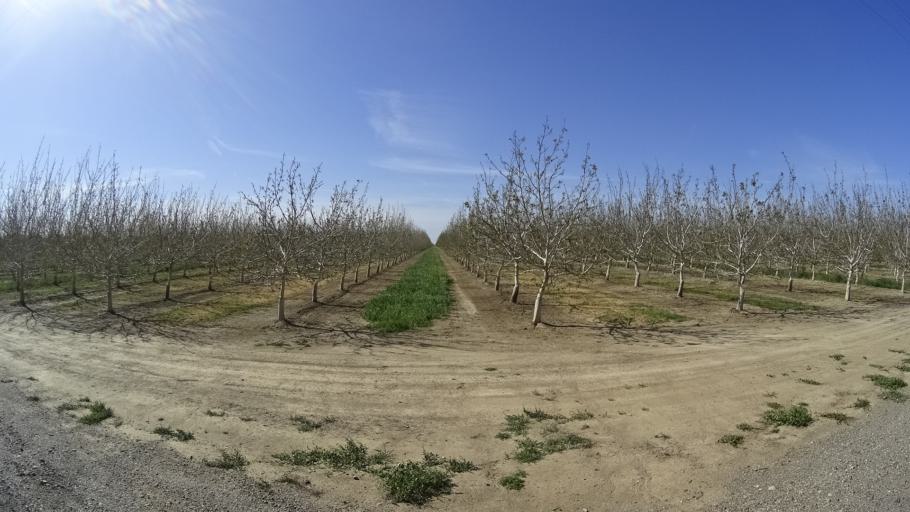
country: US
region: California
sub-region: Glenn County
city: Willows
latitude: 39.6113
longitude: -122.1878
